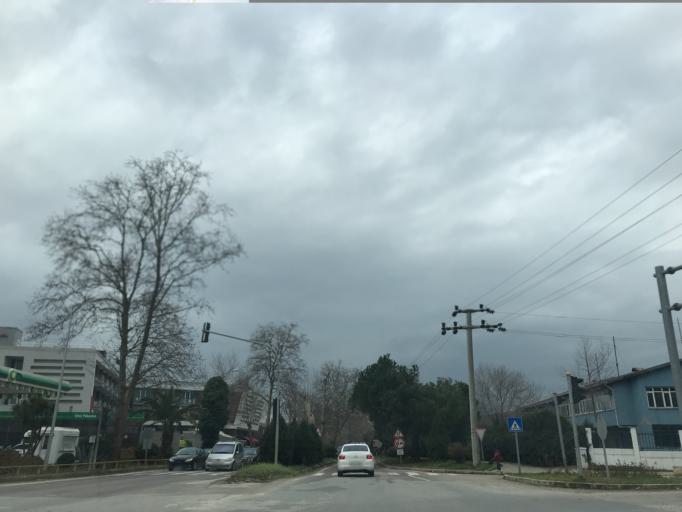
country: TR
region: Yalova
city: Kadikoy
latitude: 40.6458
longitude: 29.2334
